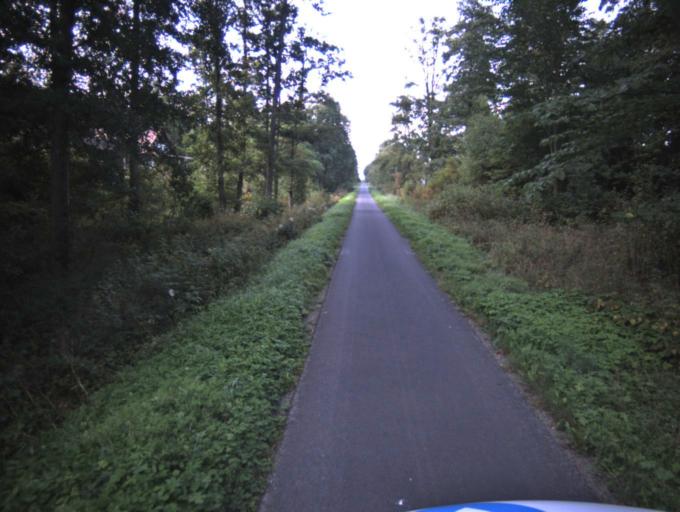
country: SE
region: Vaestra Goetaland
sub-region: Ulricehamns Kommun
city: Ulricehamn
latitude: 57.7180
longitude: 13.3979
